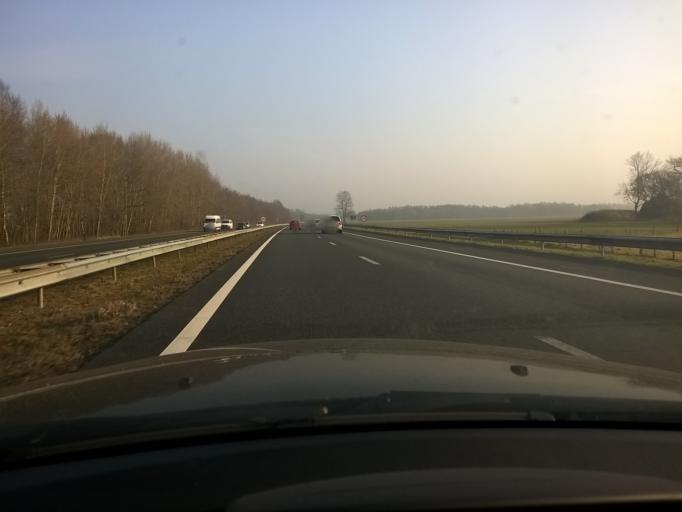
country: NL
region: Drenthe
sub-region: Gemeente Tynaarlo
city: Tynaarlo
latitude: 53.0884
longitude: 6.6053
